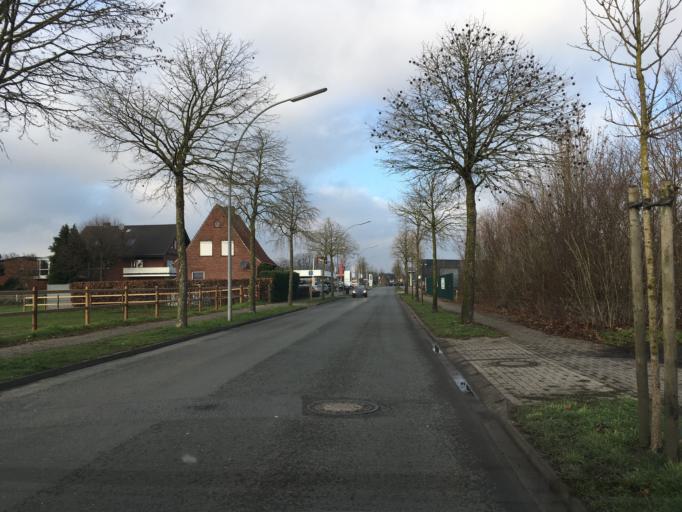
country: DE
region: North Rhine-Westphalia
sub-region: Regierungsbezirk Munster
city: Gescher
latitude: 51.9594
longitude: 6.9911
